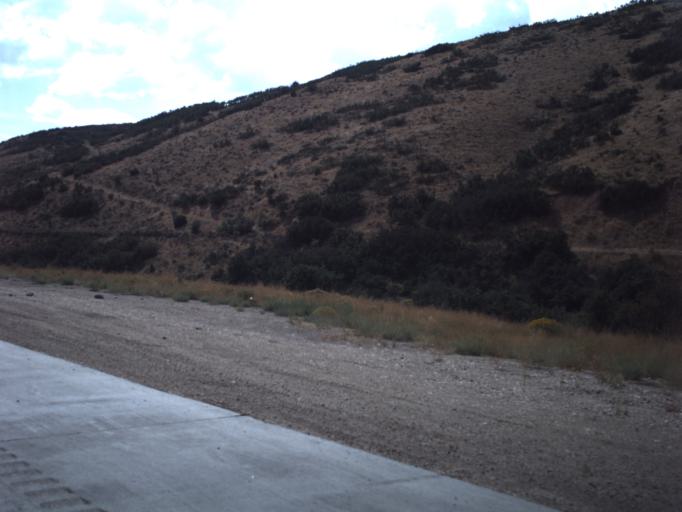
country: US
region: Utah
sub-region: Summit County
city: Coalville
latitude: 40.7961
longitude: -111.4479
